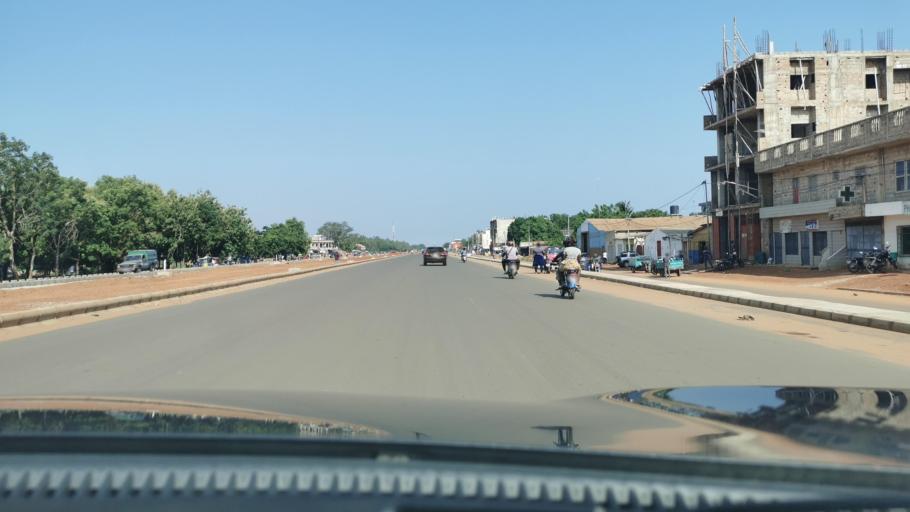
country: TG
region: Maritime
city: Lome
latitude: 6.1960
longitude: 1.1540
